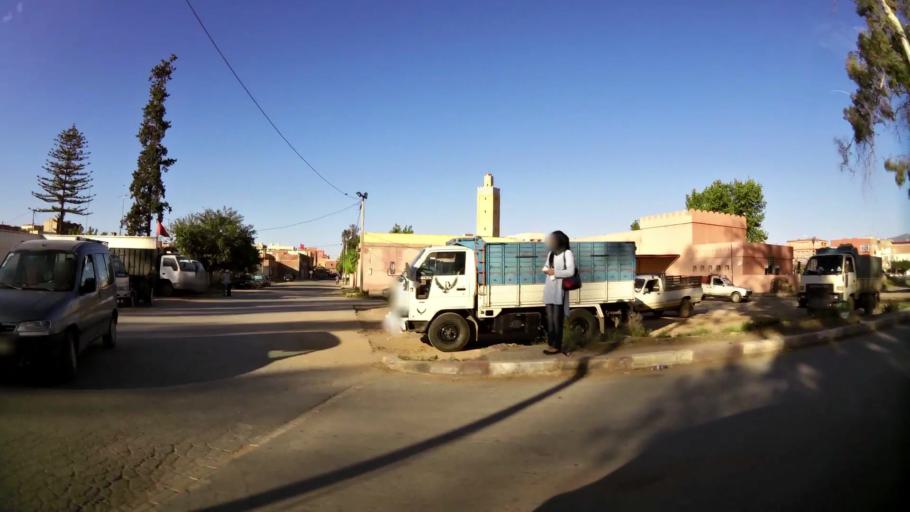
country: MA
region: Oriental
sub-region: Berkane-Taourirt
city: Berkane
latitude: 34.9226
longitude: -2.3391
